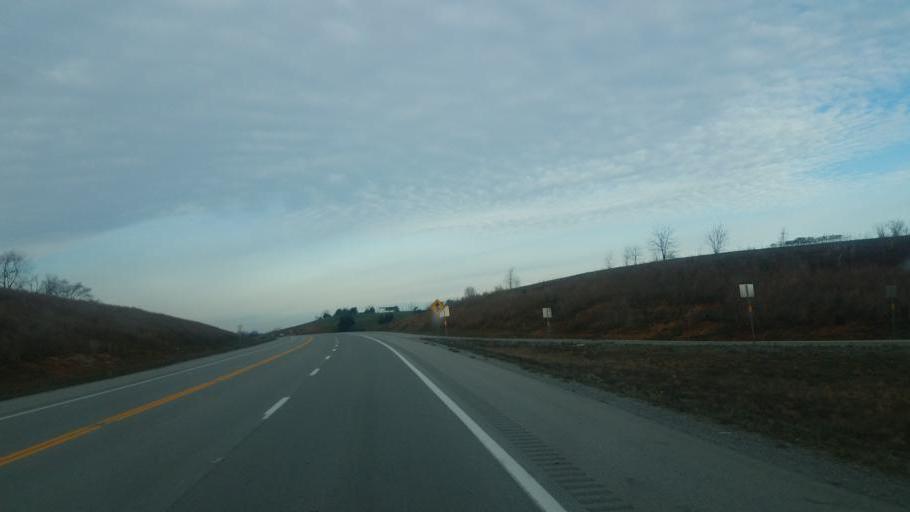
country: US
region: Kentucky
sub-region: Clinton County
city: Albany
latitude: 36.6624
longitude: -85.1173
